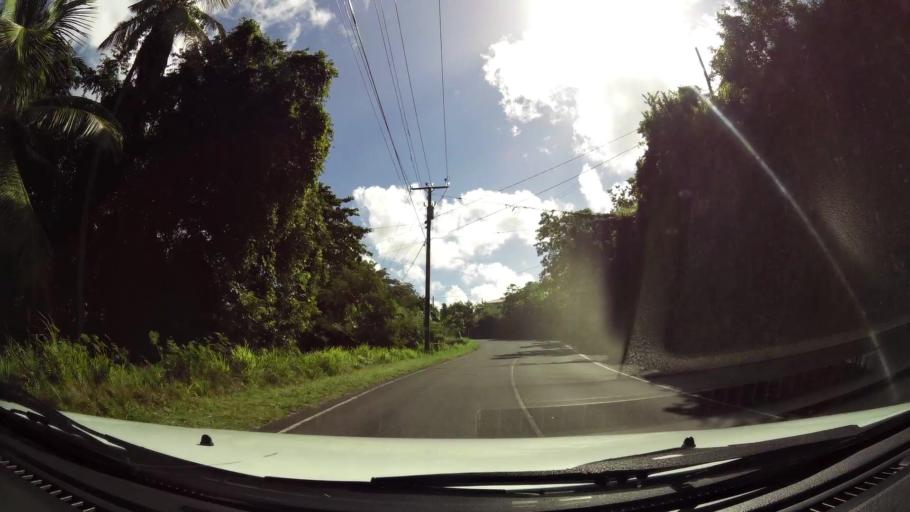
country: LC
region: Choiseul Quarter
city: Choiseul
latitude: 13.7717
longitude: -61.0468
